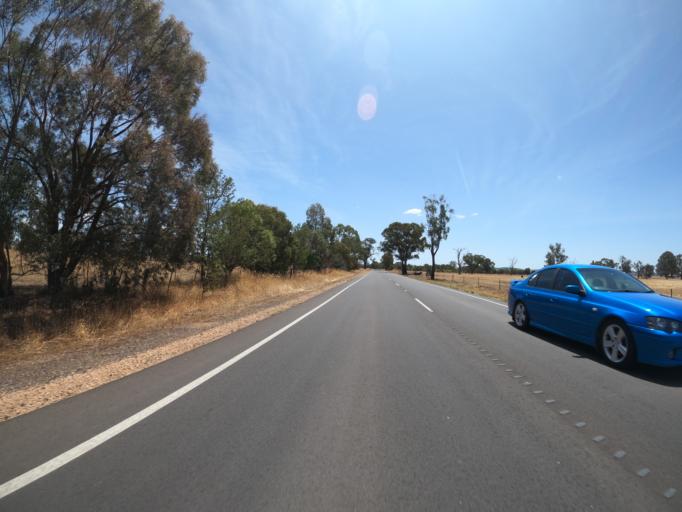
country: AU
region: Victoria
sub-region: Benalla
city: Benalla
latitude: -36.5022
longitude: 146.0230
